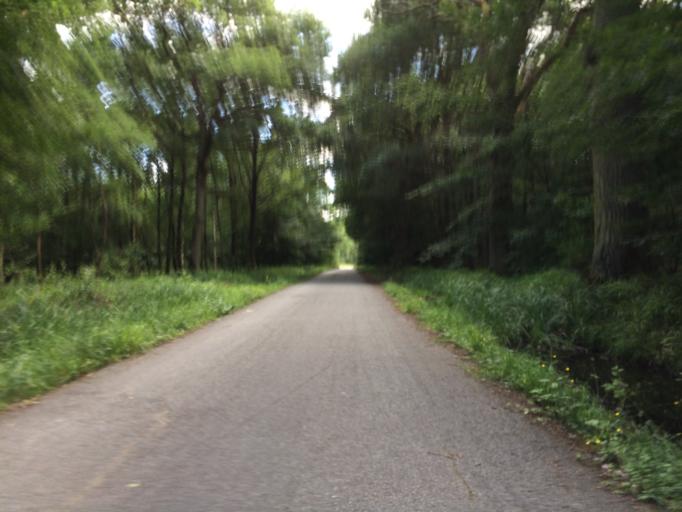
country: FR
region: Ile-de-France
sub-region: Departement de l'Essonne
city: Brunoy
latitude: 48.6688
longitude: 2.4857
